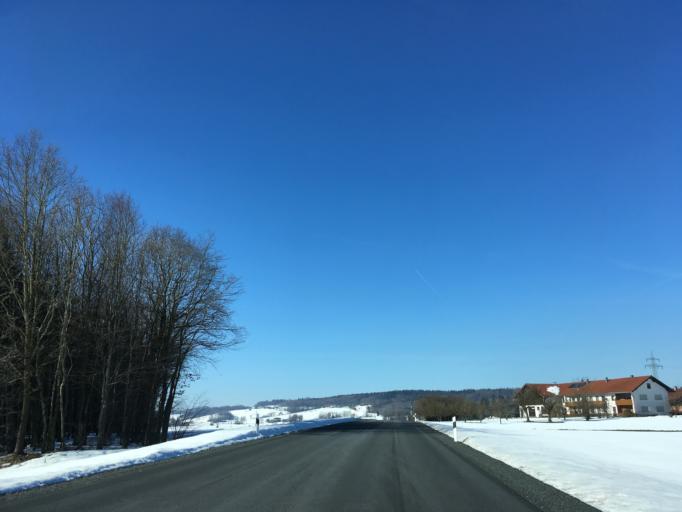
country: DE
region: Bavaria
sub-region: Upper Bavaria
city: Albaching
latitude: 48.1141
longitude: 12.0995
